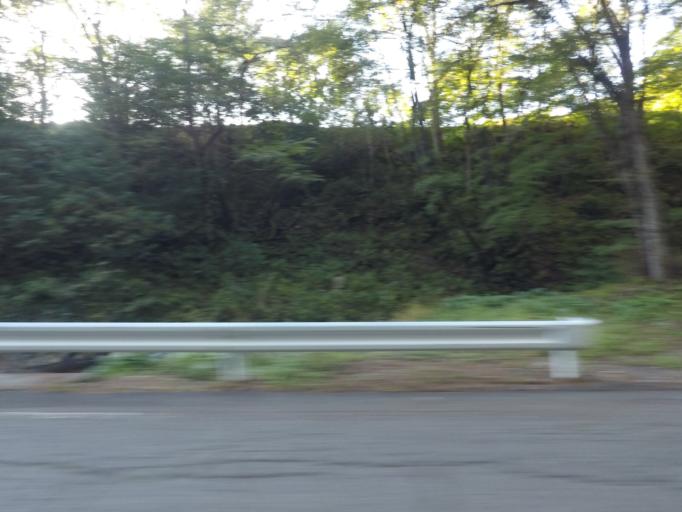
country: JP
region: Nagano
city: Ina
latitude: 35.9659
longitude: 137.7508
